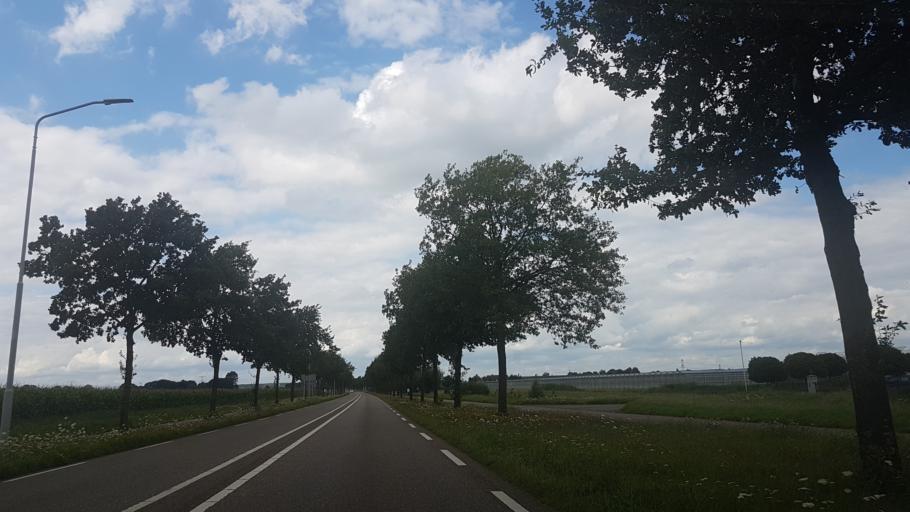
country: NL
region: North Brabant
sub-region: Gemeente Made en Drimmelen
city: Made
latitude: 51.6820
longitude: 4.8170
